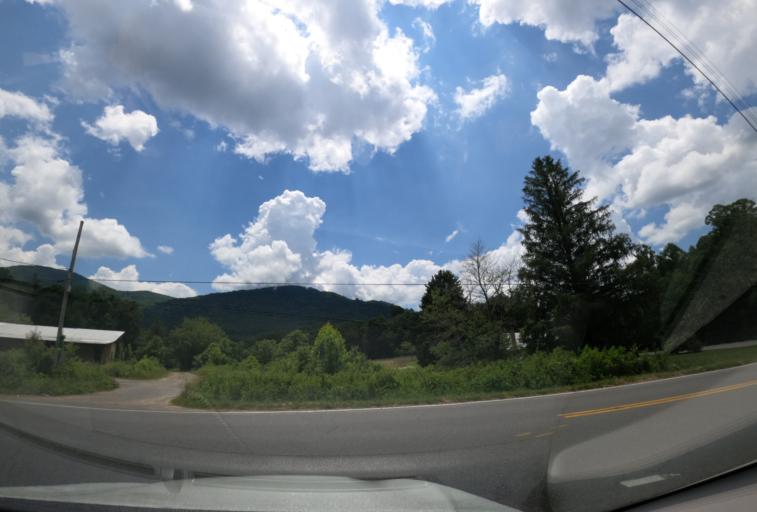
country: US
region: North Carolina
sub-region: Haywood County
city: Waynesville
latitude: 35.4764
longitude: -82.9627
